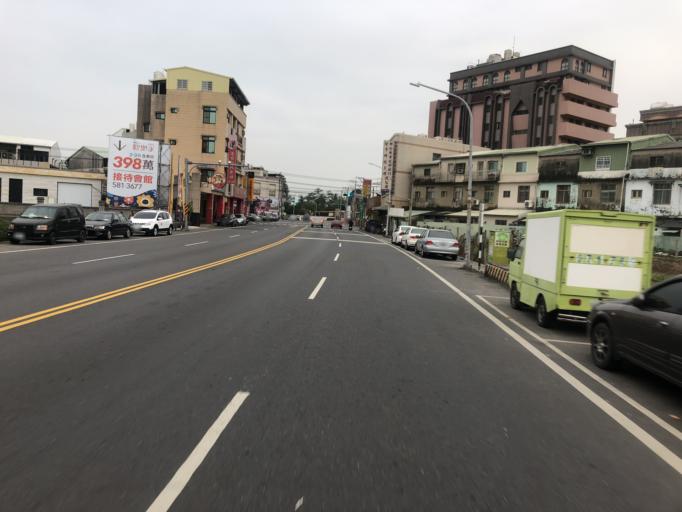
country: TW
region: Taiwan
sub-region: Tainan
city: Tainan
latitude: 23.1285
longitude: 120.2863
